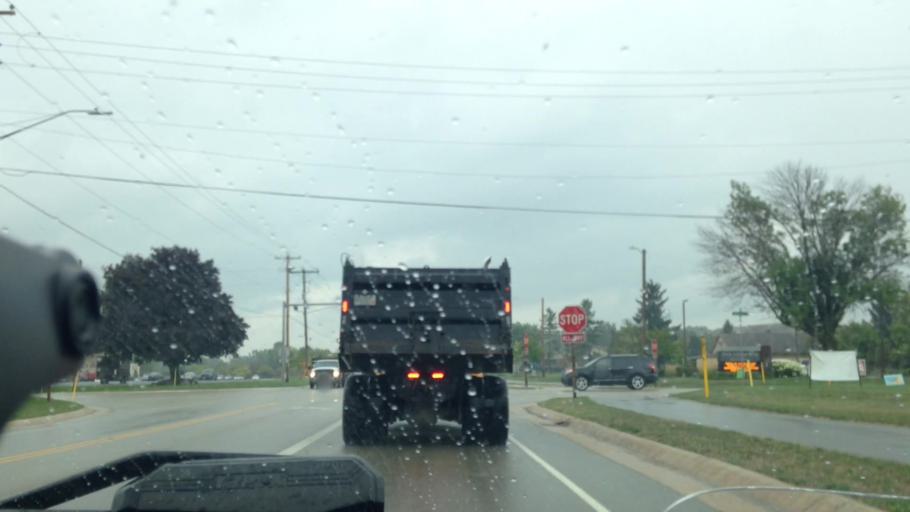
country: US
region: Wisconsin
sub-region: Washington County
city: Richfield
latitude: 43.2367
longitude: -88.1866
